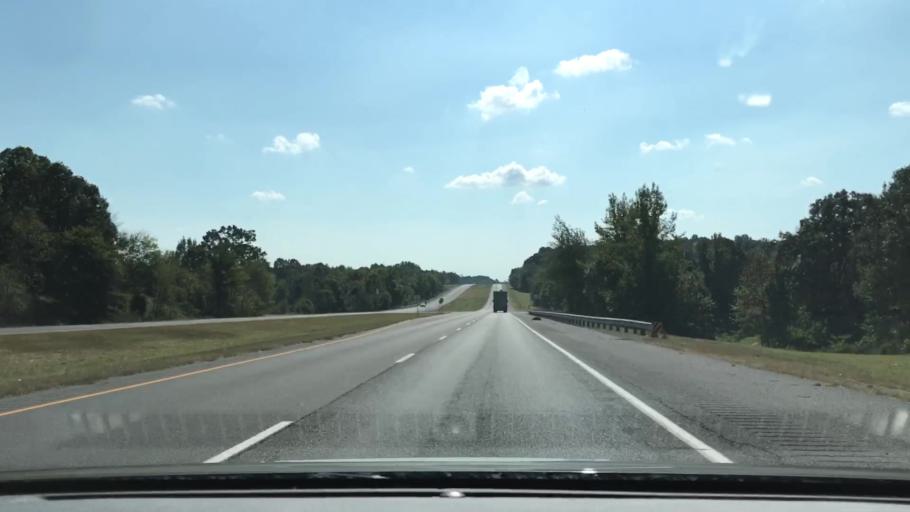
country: US
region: Kentucky
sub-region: Marshall County
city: Benton
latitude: 36.7764
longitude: -88.3204
